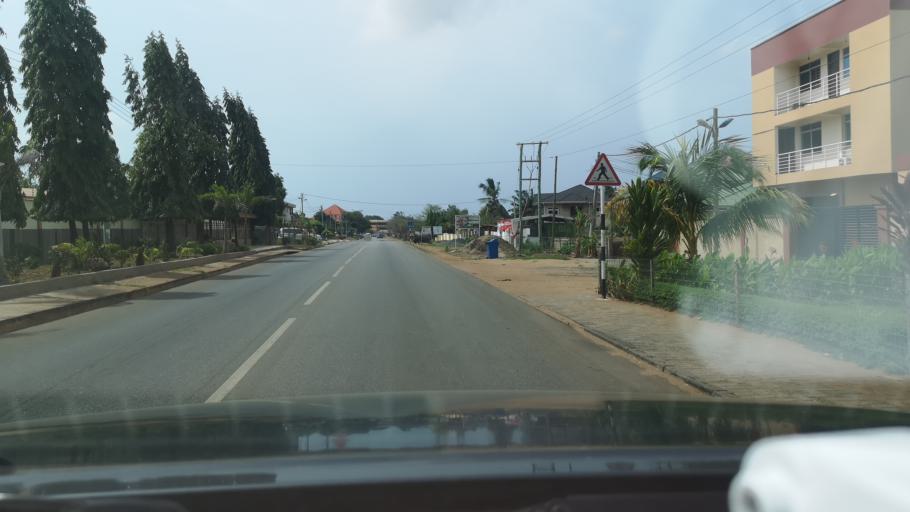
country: GH
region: Greater Accra
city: Tema
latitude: 5.6720
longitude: -0.0286
